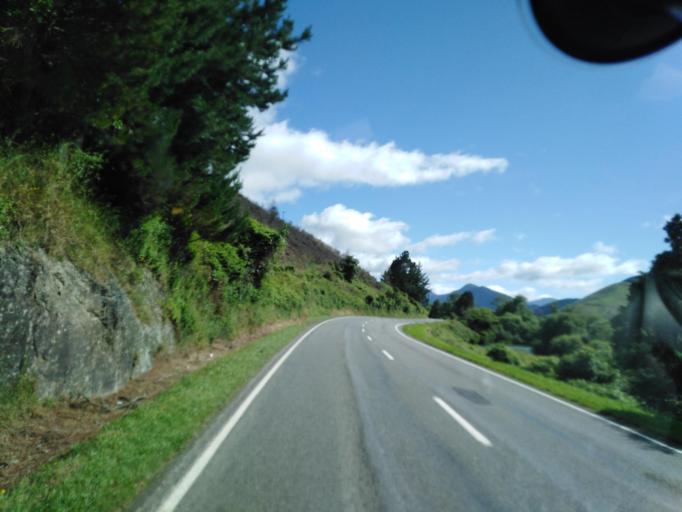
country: NZ
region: Nelson
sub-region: Nelson City
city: Nelson
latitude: -41.2559
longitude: 173.5763
